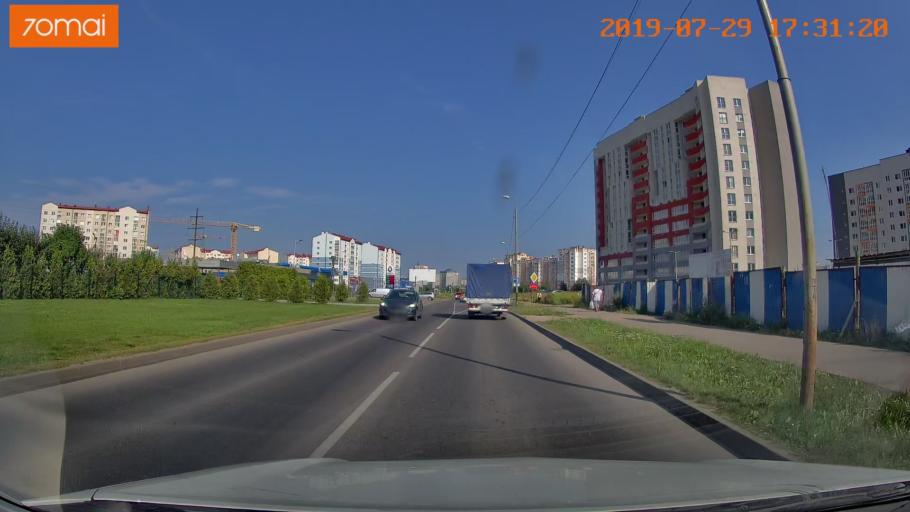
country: RU
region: Kaliningrad
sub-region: Gorod Kaliningrad
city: Kaliningrad
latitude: 54.7475
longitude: 20.4866
